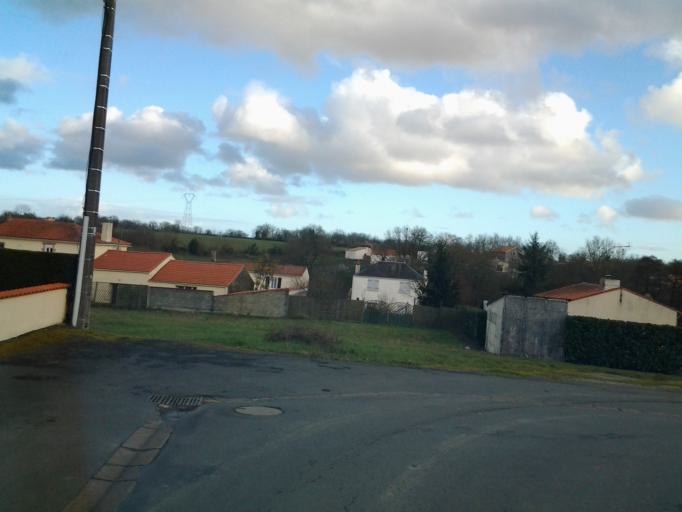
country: FR
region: Pays de la Loire
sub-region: Departement de la Vendee
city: Chateau-Guibert
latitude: 46.6136
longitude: -1.2385
